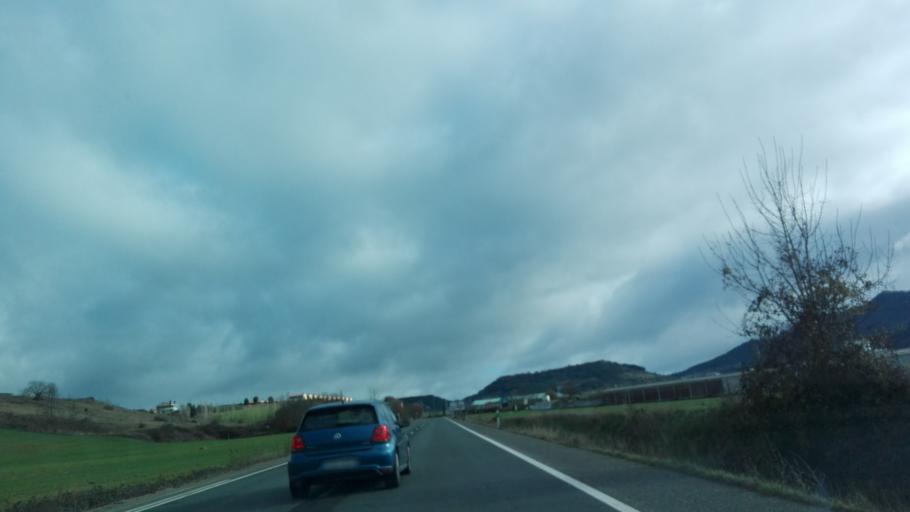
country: ES
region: Navarre
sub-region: Provincia de Navarra
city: Egues-Uharte
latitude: 42.8268
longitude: -1.5660
